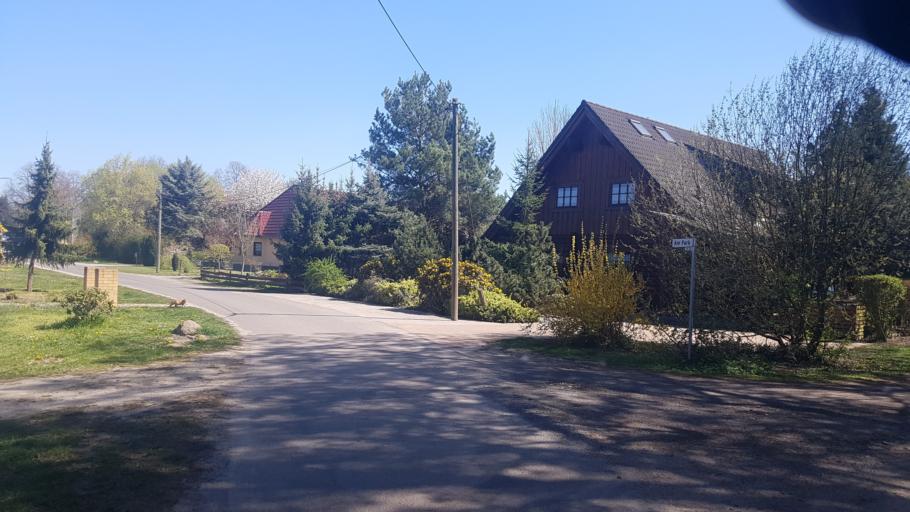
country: DE
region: Brandenburg
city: Sonnewalde
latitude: 51.7120
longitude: 13.6285
